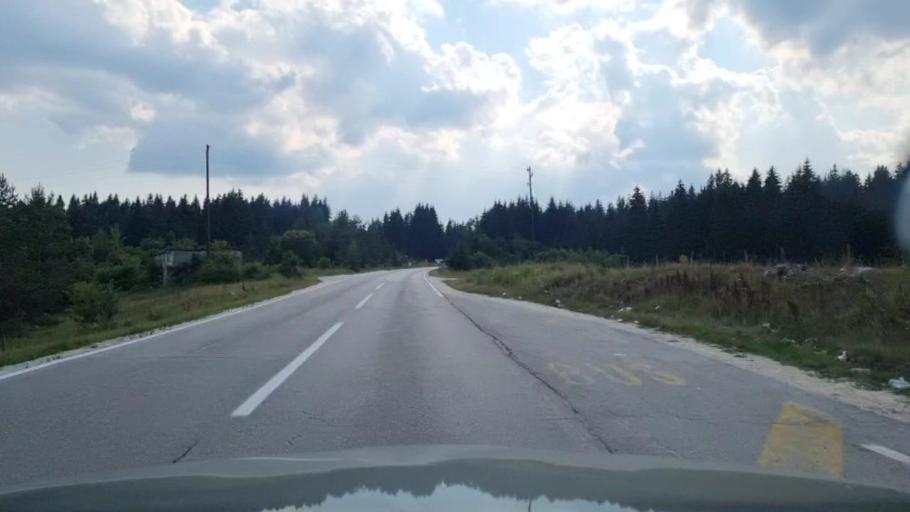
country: BA
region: Federation of Bosnia and Herzegovina
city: Olovo
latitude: 44.0782
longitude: 18.5099
